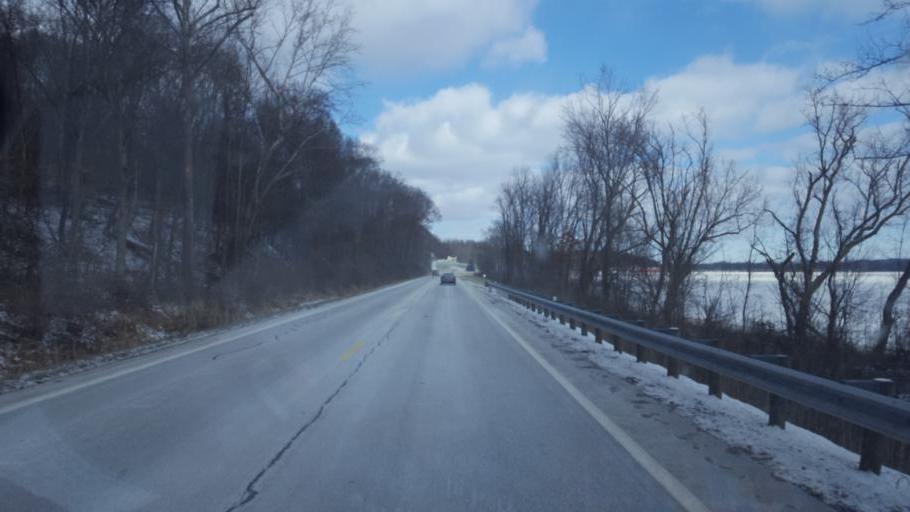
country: US
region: Ohio
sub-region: Coshocton County
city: Coshocton
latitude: 40.2243
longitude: -81.8813
